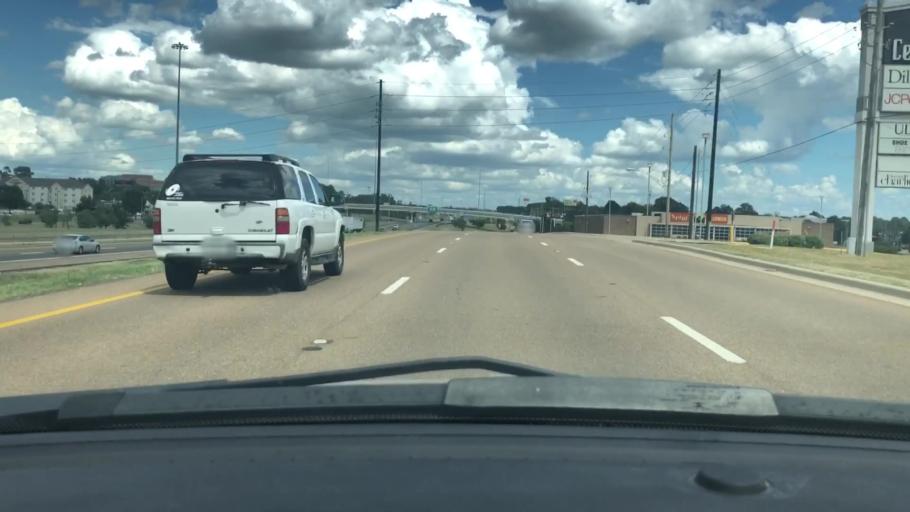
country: US
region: Texas
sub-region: Bowie County
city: Wake Village
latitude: 33.4584
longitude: -94.0813
